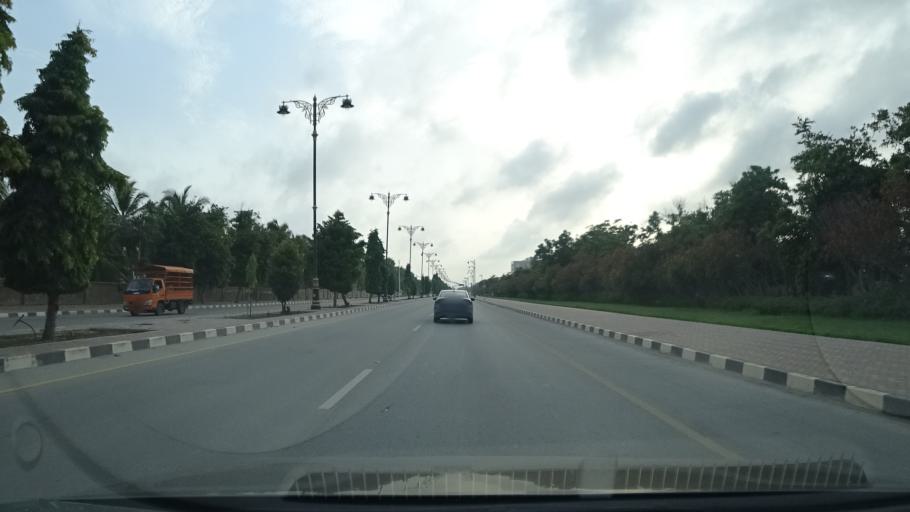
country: OM
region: Zufar
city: Salalah
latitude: 17.0260
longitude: 54.1654
